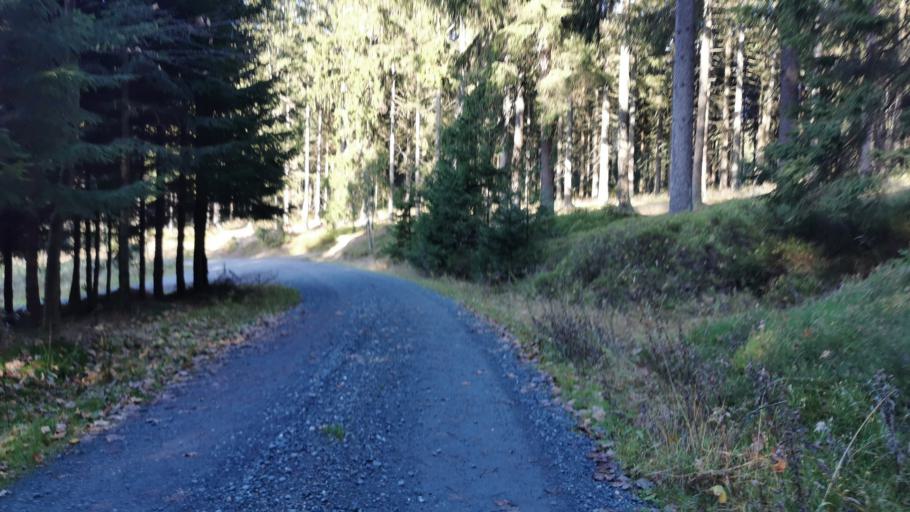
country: DE
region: Bavaria
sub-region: Upper Franconia
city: Reichenbach
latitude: 50.4374
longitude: 11.4332
